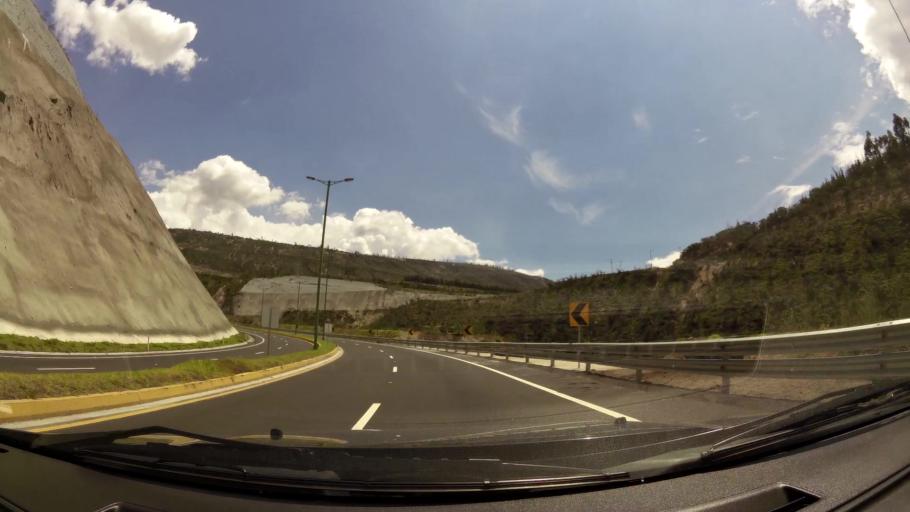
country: EC
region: Pichincha
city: Quito
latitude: -0.0928
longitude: -78.3917
